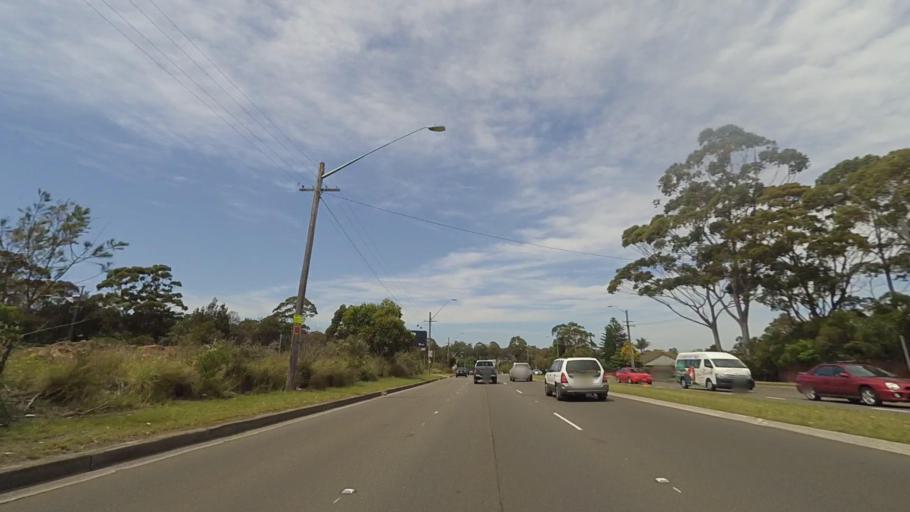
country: AU
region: New South Wales
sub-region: Sutherland Shire
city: Heathcote
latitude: -34.0800
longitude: 151.0109
